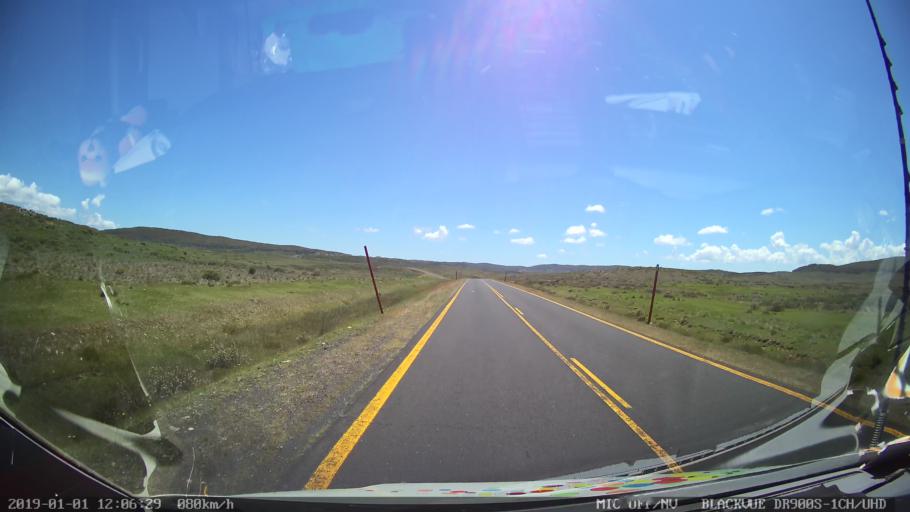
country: AU
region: New South Wales
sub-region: Snowy River
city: Jindabyne
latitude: -35.8443
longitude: 148.4914
